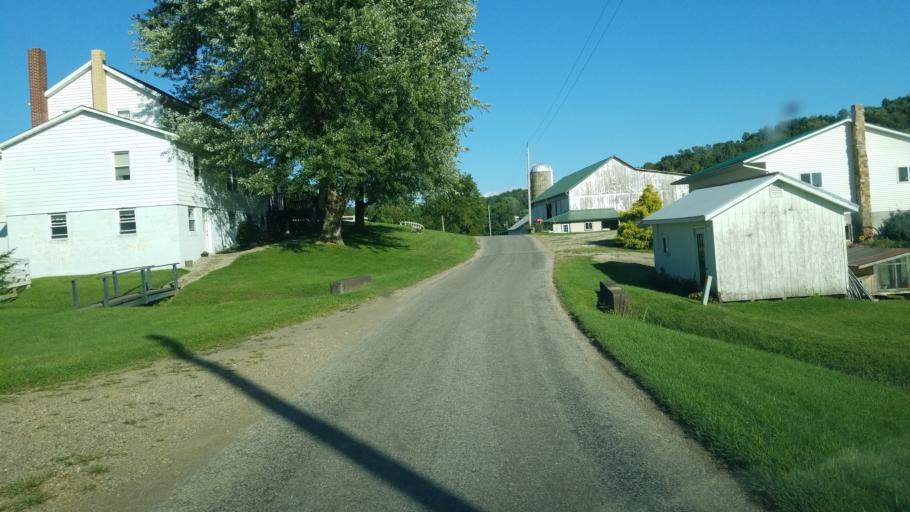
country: US
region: Ohio
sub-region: Holmes County
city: Millersburg
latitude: 40.6026
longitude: -81.8971
